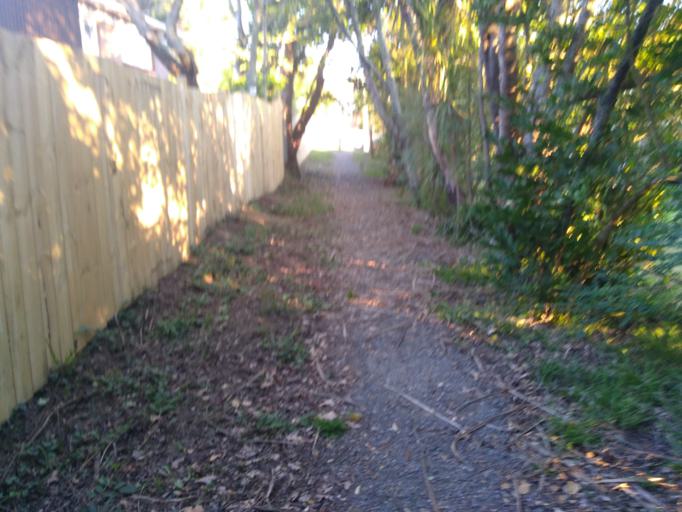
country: NZ
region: Auckland
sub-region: Auckland
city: Rosebank
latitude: -36.8599
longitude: 174.6396
